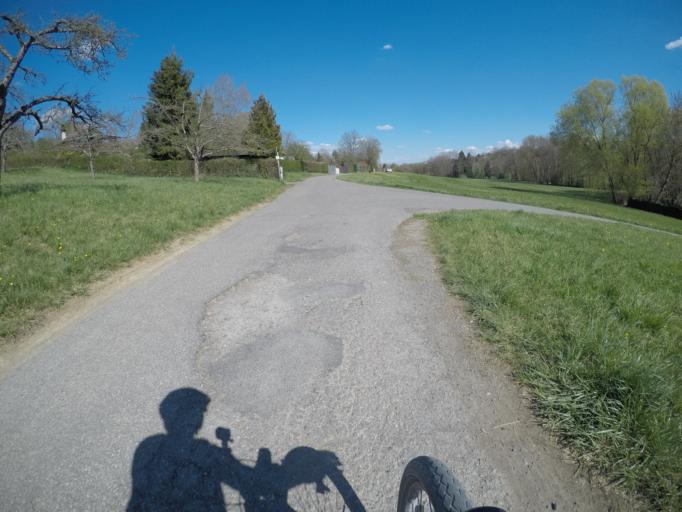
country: DE
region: Baden-Wuerttemberg
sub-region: Regierungsbezirk Stuttgart
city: Weil im Schonbuch
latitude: 48.6280
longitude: 9.0726
